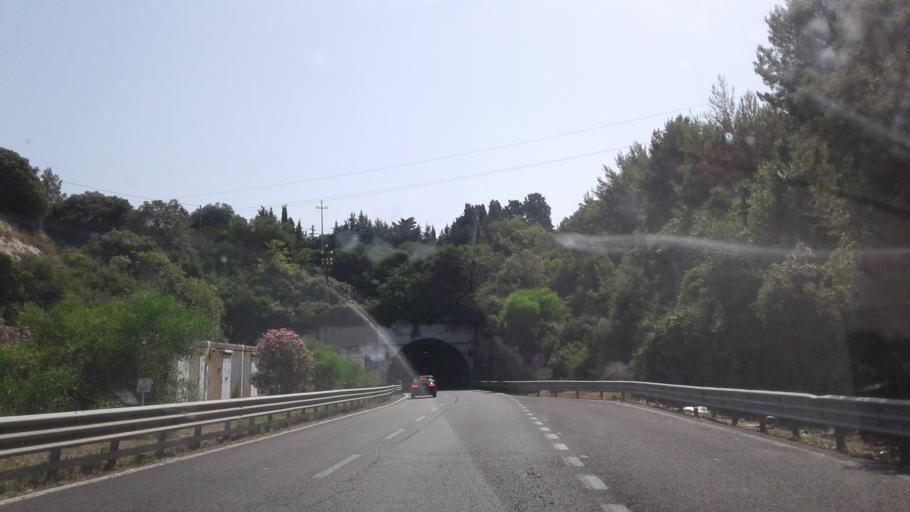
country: IT
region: Sardinia
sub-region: Provincia di Sassari
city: Tissi
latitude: 40.6980
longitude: 8.5677
